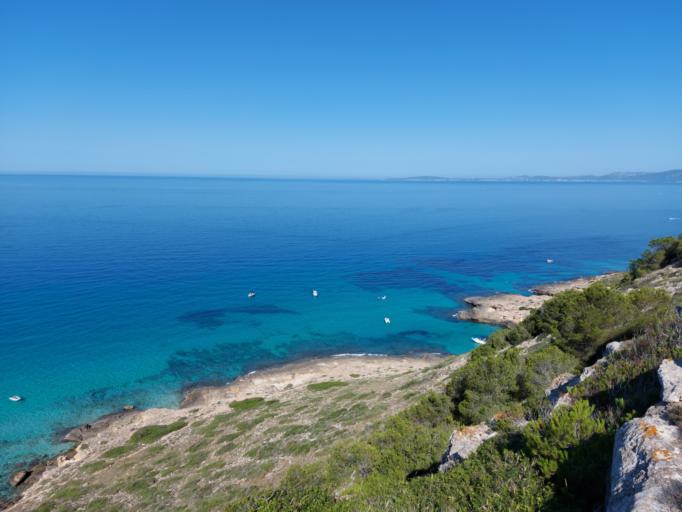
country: ES
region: Balearic Islands
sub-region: Illes Balears
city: s'Arenal
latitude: 39.4574
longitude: 2.7393
